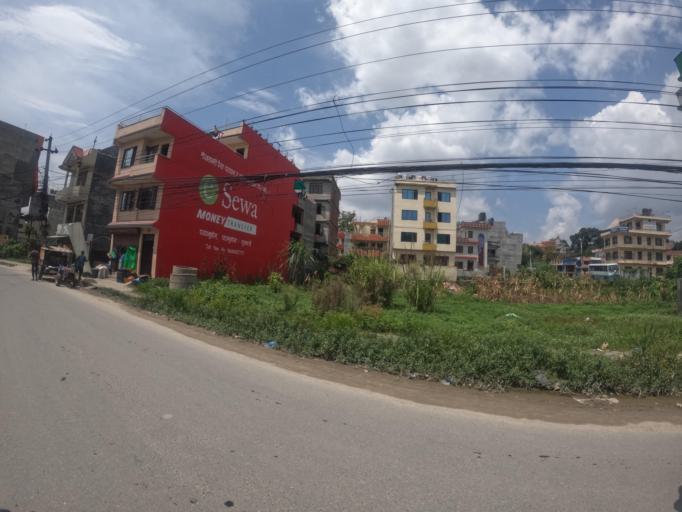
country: NP
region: Central Region
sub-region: Bagmati Zone
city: Bhaktapur
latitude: 27.6767
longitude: 85.3824
